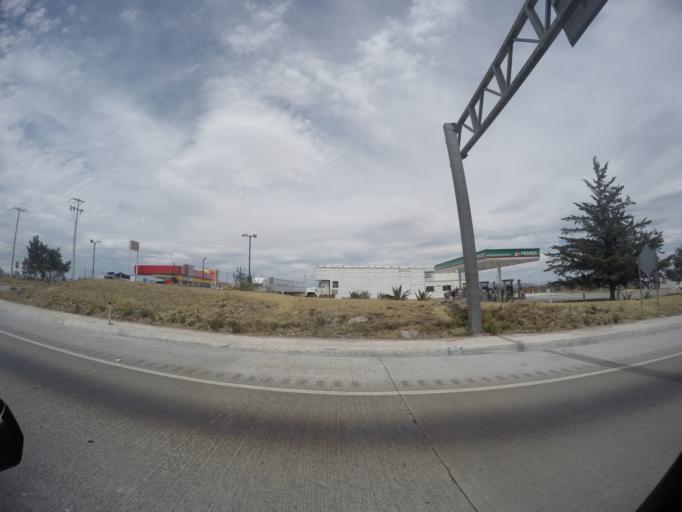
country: MX
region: Mexico
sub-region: Jilotepec
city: La Comunidad
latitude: 20.0368
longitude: -99.5627
